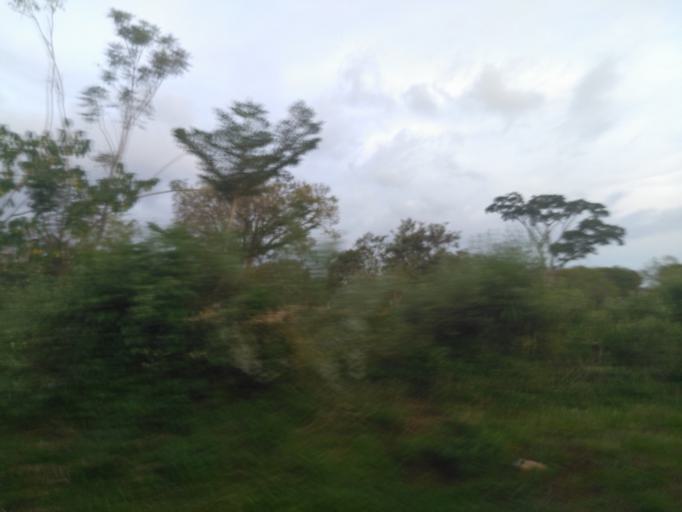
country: UG
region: Eastern Region
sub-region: Jinja District
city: Jinja
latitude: 0.4258
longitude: 33.1979
